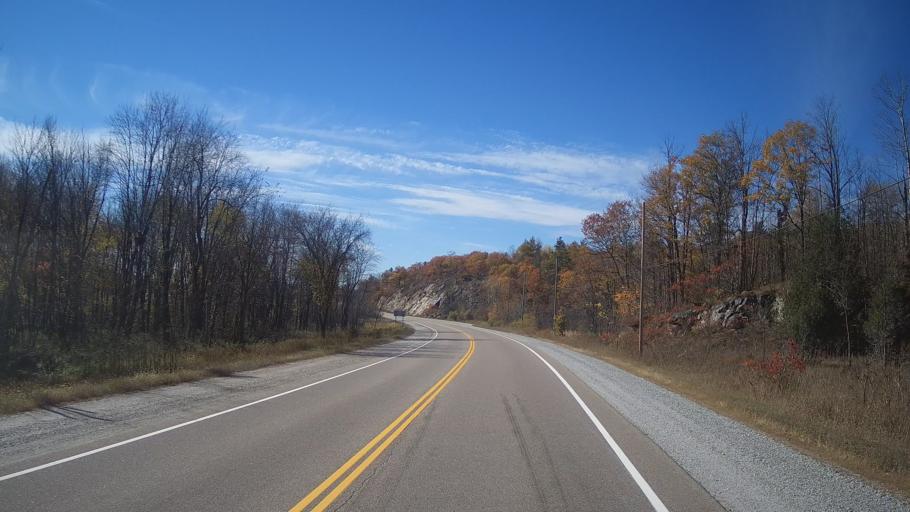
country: CA
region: Ontario
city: Perth
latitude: 44.8441
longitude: -76.4937
